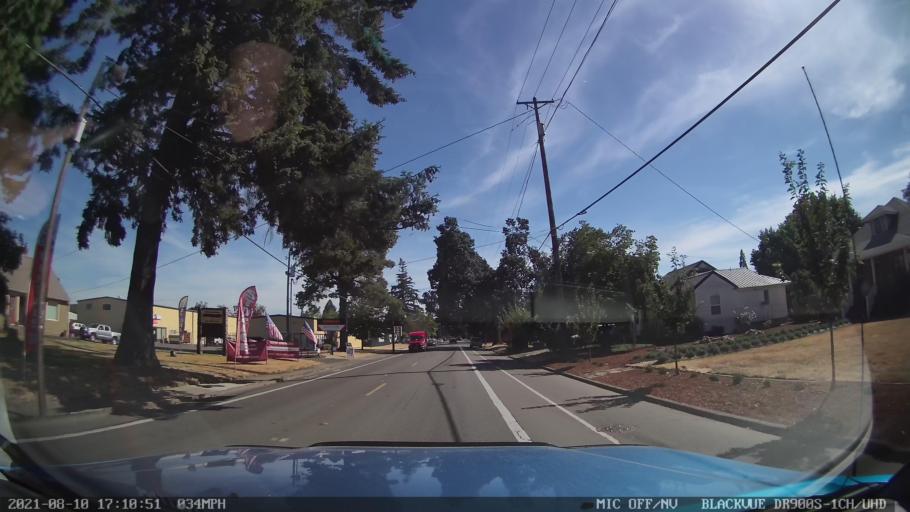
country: US
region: Oregon
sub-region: Marion County
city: Salem
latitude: 44.9641
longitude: -123.0195
